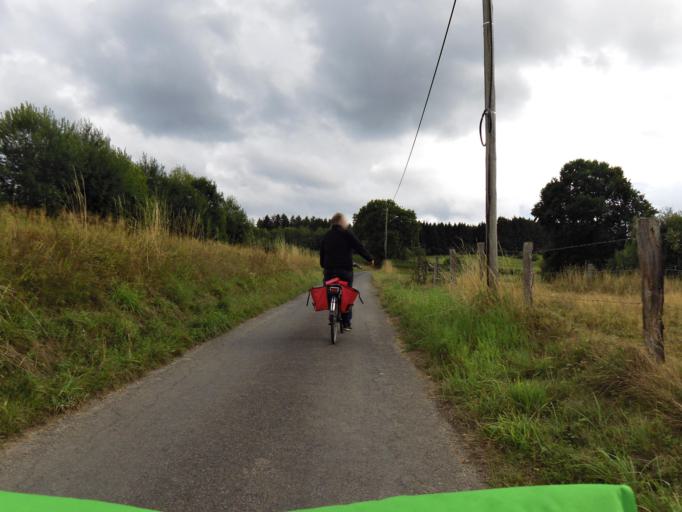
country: BE
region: Wallonia
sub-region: Province de Namur
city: Bievre
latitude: 49.8876
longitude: 5.0042
